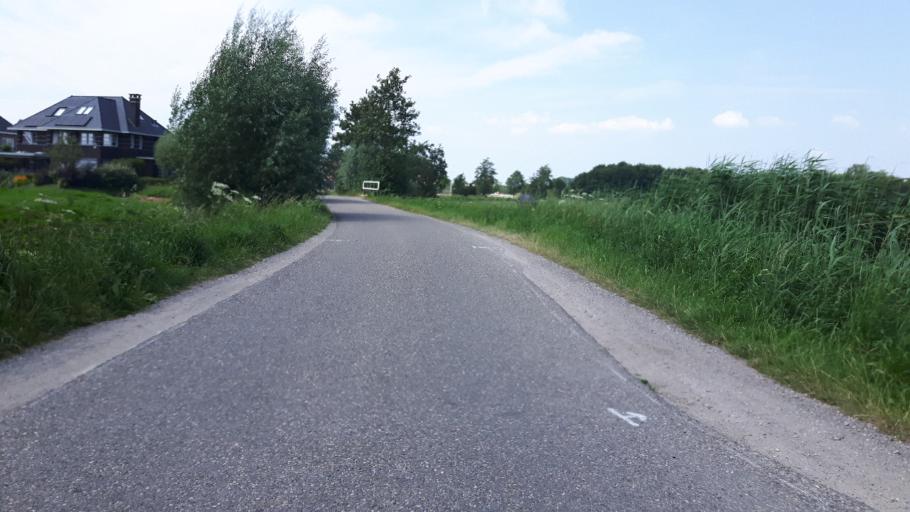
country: NL
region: South Holland
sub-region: Molenwaard
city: Liesveld
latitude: 51.9229
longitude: 4.8379
